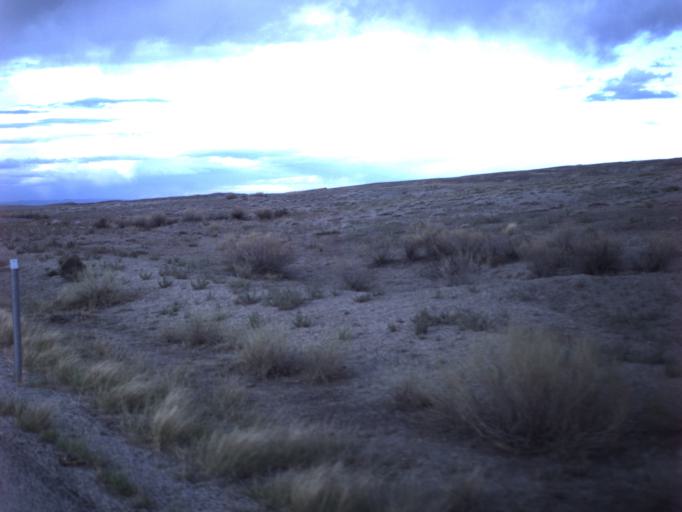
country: US
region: Utah
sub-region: Grand County
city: Moab
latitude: 38.8826
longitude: -109.3120
